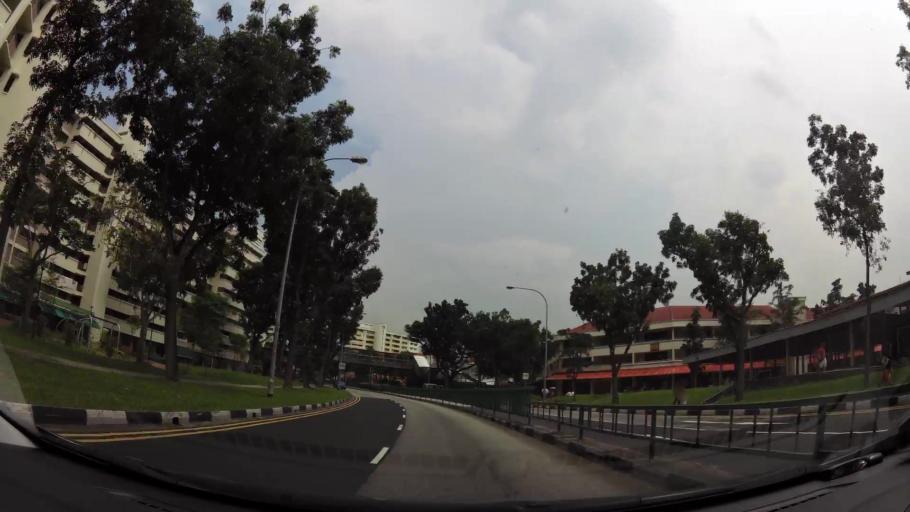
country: SG
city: Singapore
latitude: 1.3327
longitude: 103.9131
